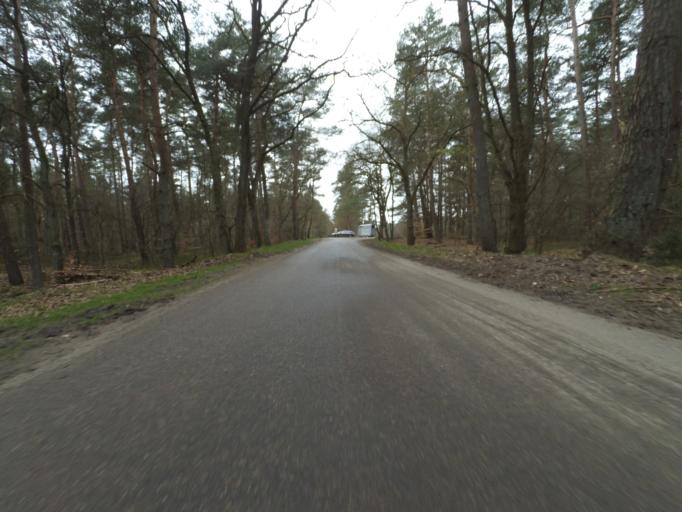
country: NL
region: Gelderland
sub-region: Gemeente Apeldoorn
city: Loenen
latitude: 52.0998
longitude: 6.0249
